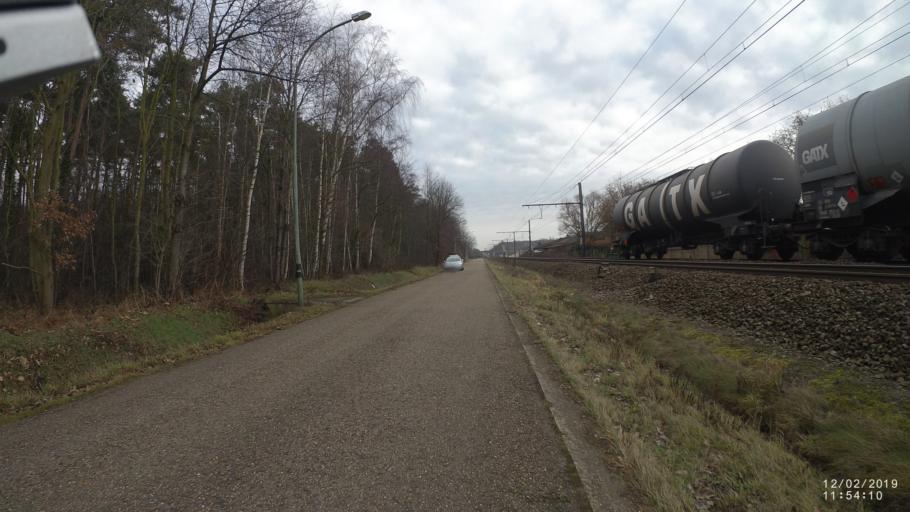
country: BE
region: Flanders
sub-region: Provincie Vlaams-Brabant
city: Aarschot
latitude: 51.0006
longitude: 4.8508
